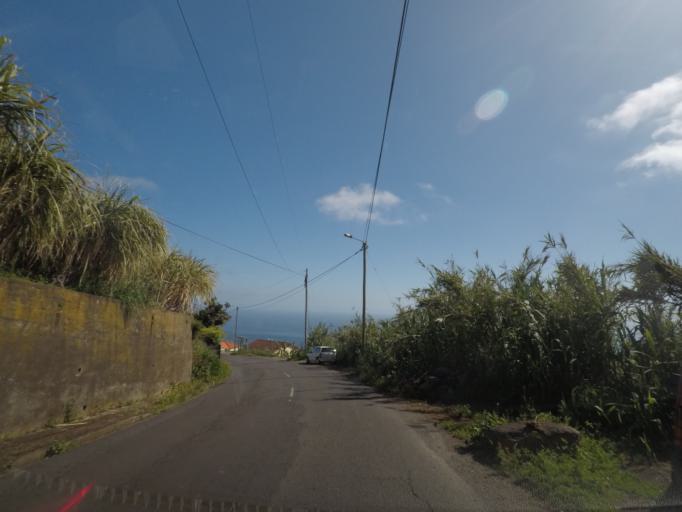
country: PT
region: Madeira
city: Ponta do Sol
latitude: 32.7003
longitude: -17.1106
